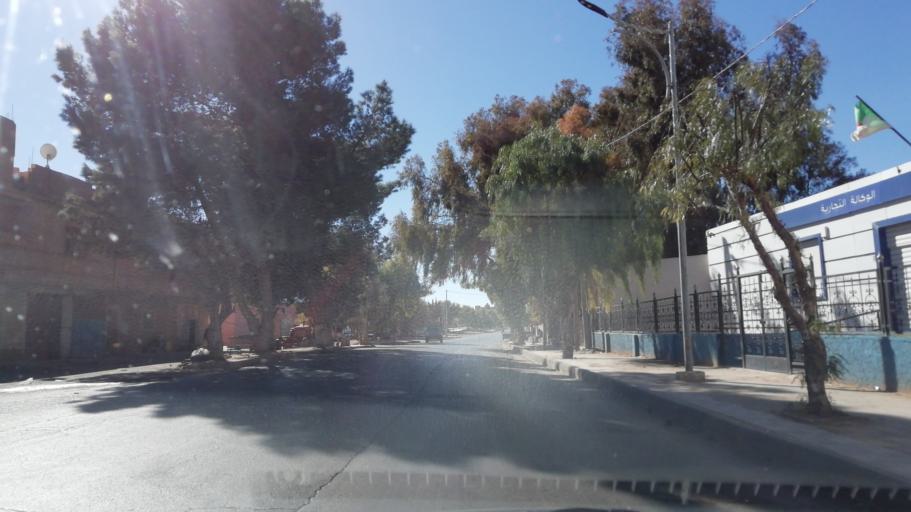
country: DZ
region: Saida
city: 'Ain el Hadjar
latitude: 34.0442
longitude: 0.0844
